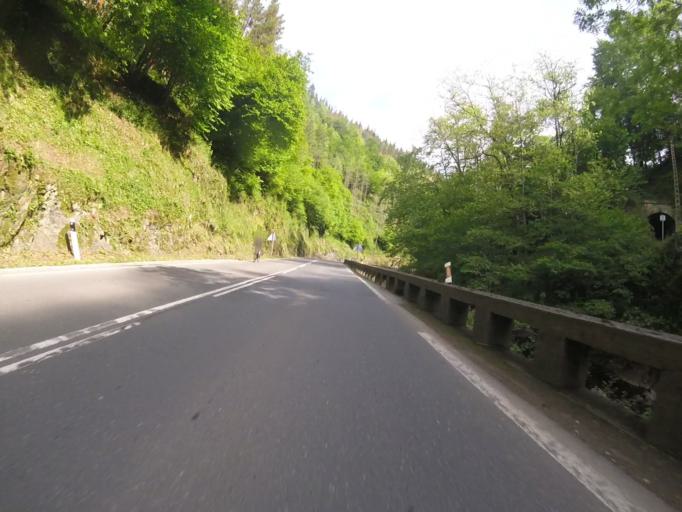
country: ES
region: Basque Country
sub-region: Provincia de Guipuzcoa
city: Azkoitia
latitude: 43.1443
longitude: -2.3465
